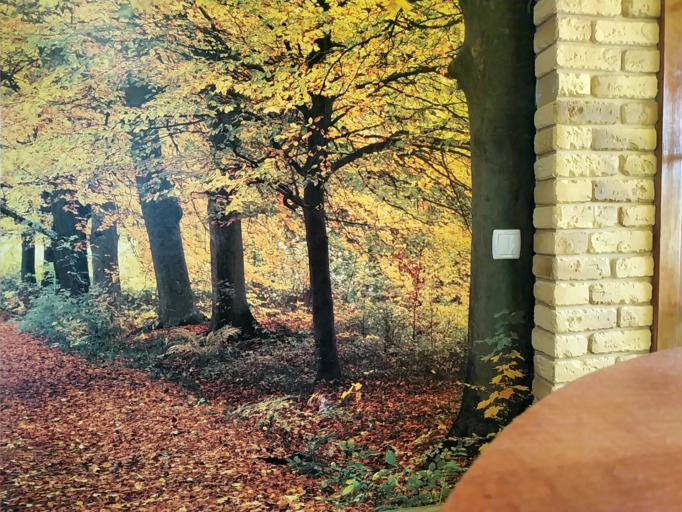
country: RU
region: Pskov
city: Dno
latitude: 57.9117
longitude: 30.1731
